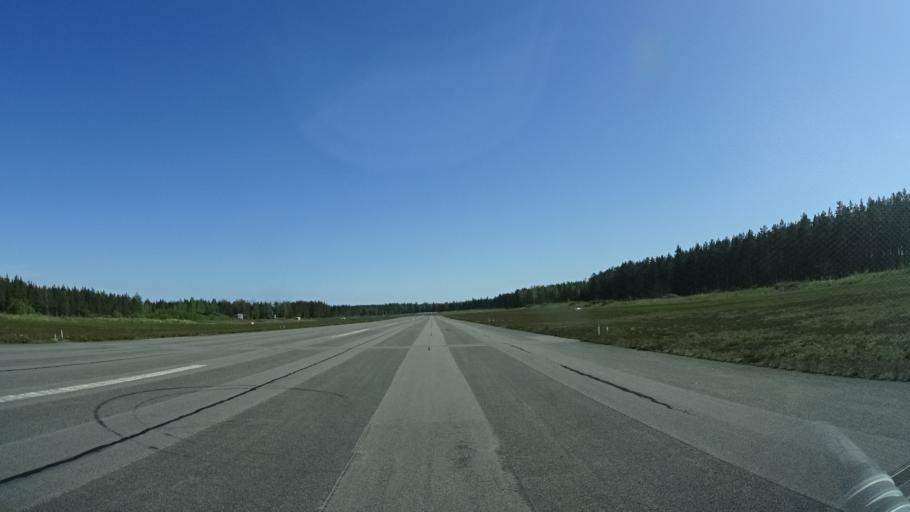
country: SE
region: Kalmar
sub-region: Vasterviks Kommun
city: Vaestervik
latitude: 57.7802
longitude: 16.5234
